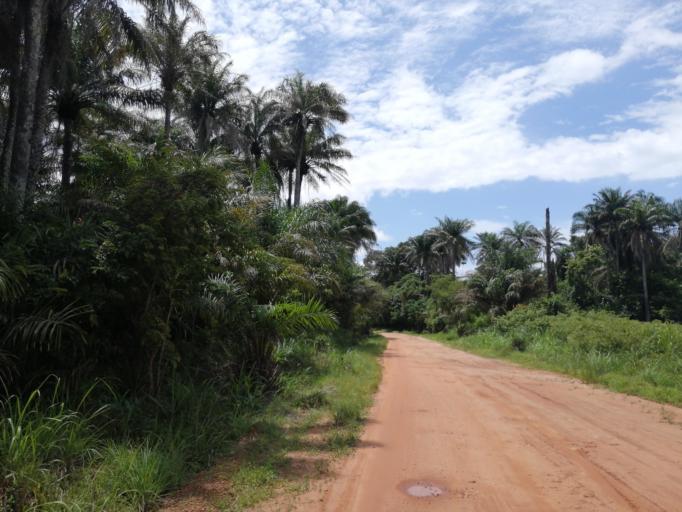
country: SL
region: Northern Province
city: Konakridee
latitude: 8.7521
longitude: -13.1438
